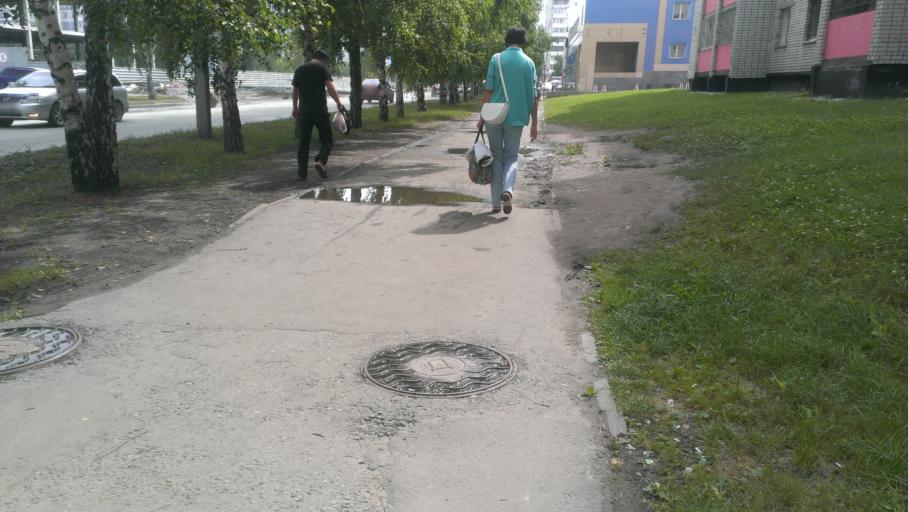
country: RU
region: Altai Krai
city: Novosilikatnyy
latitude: 53.3368
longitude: 83.6772
